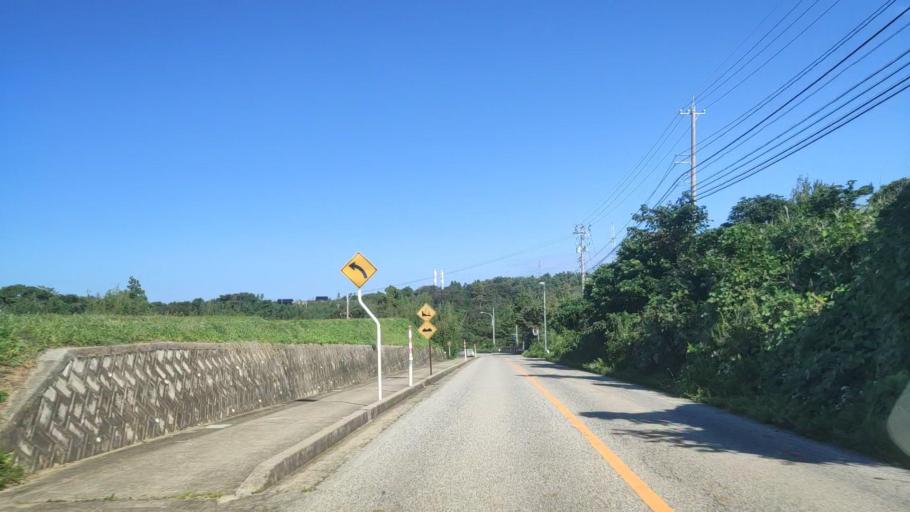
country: JP
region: Ishikawa
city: Hakui
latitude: 37.0495
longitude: 136.7361
